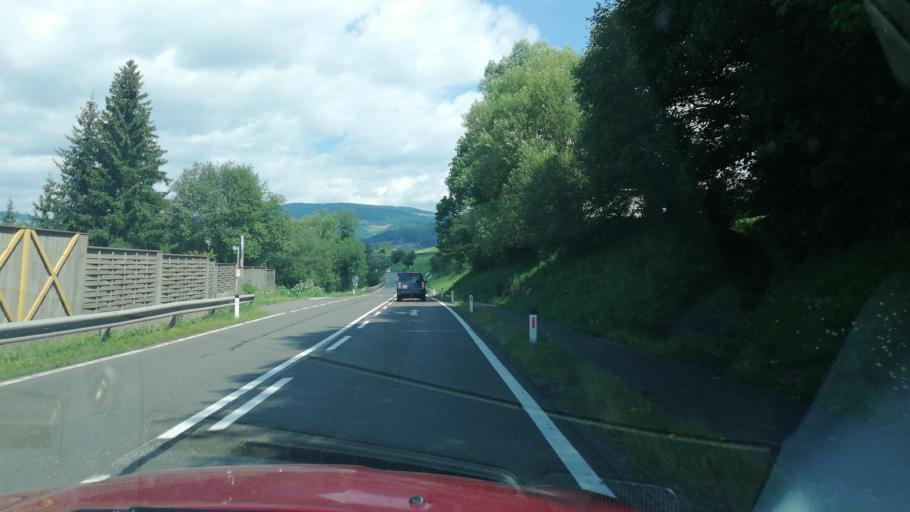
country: AT
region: Styria
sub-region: Politischer Bezirk Murau
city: Sankt Marein bei Neumarkt
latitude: 47.0546
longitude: 14.4333
